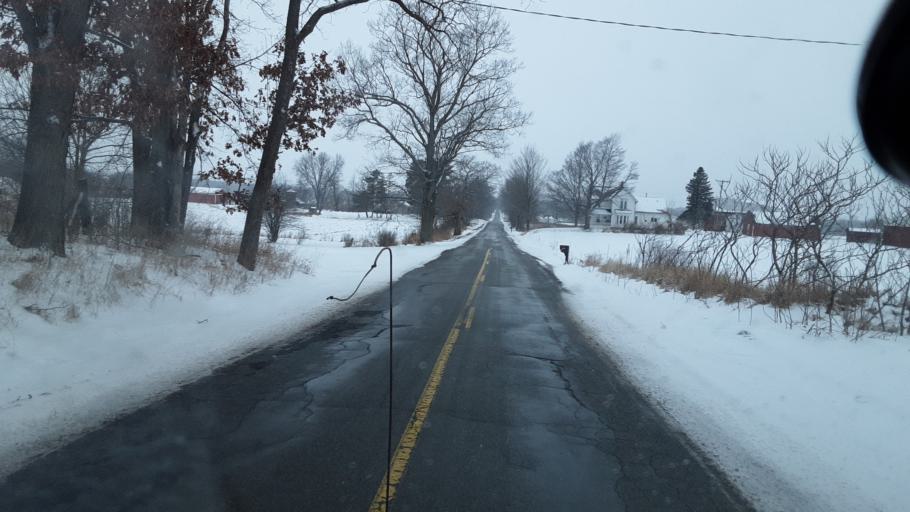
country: US
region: Michigan
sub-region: Ingham County
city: Leslie
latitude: 42.4367
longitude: -84.4674
